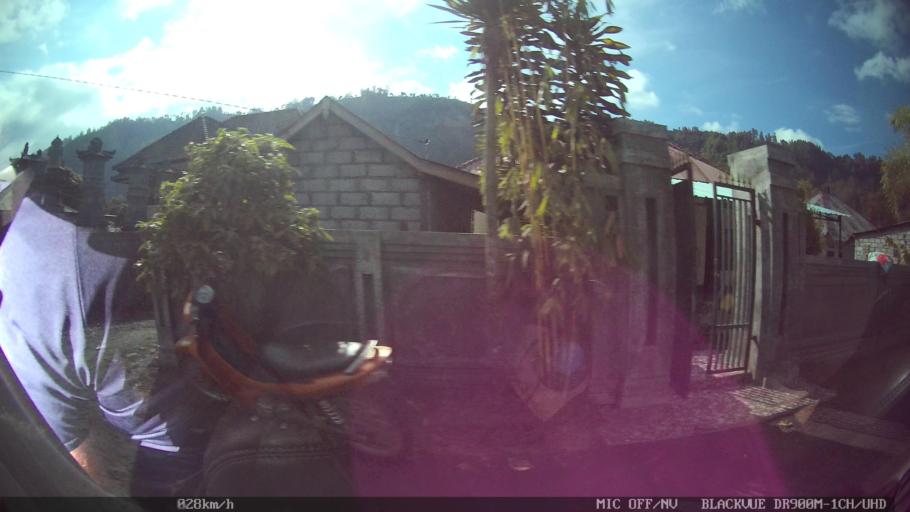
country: ID
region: Bali
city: Banjar Kedisan
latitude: -8.2162
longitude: 115.3688
